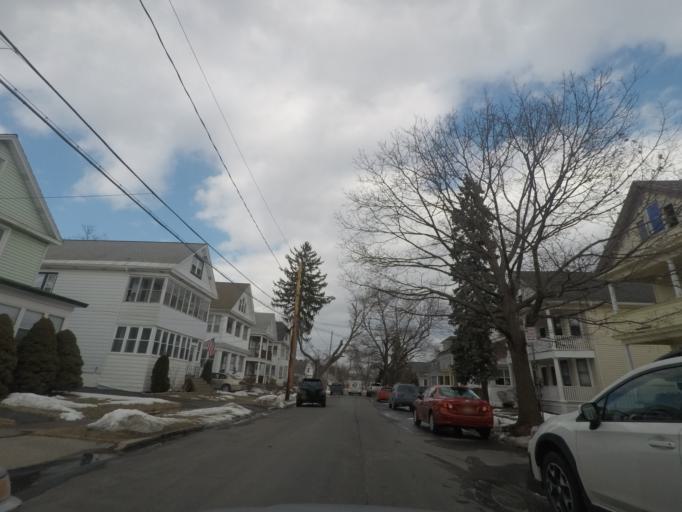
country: US
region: New York
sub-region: Albany County
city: West Albany
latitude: 42.6552
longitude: -73.7941
